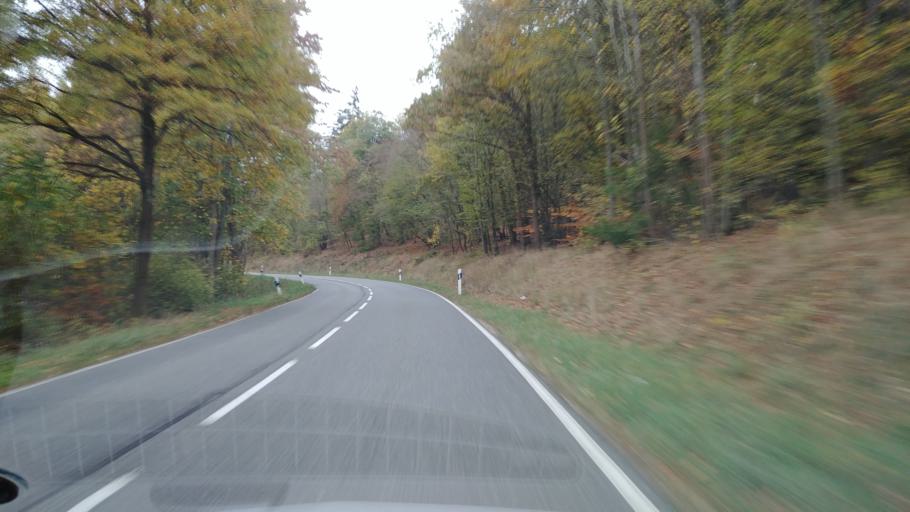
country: DE
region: Hesse
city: Taunusstein
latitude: 50.1525
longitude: 8.1615
